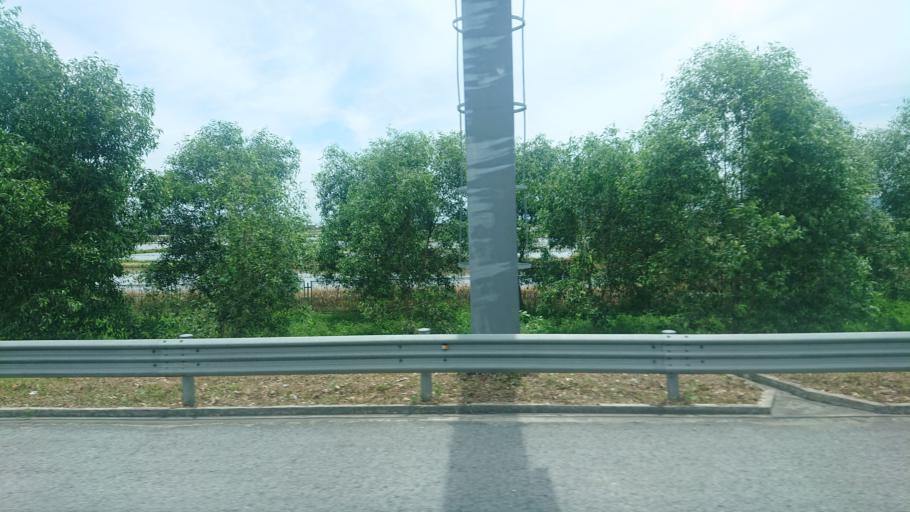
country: VN
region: Hai Phong
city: An Lao
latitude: 20.7984
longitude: 106.5389
